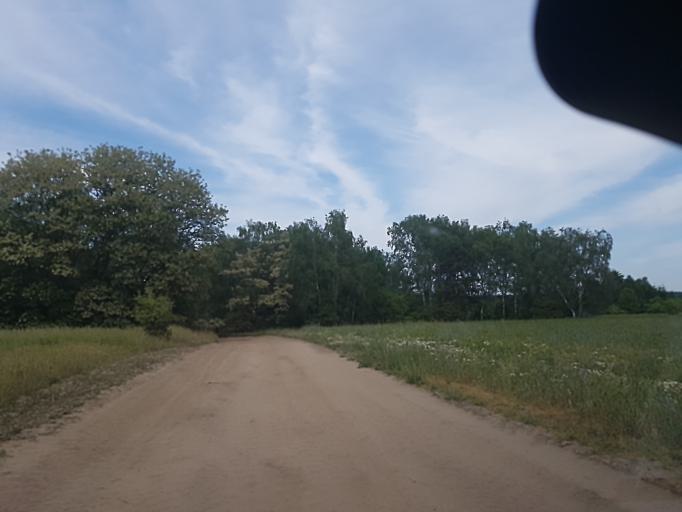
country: DE
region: Brandenburg
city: Gorzke
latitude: 52.1073
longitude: 12.3826
